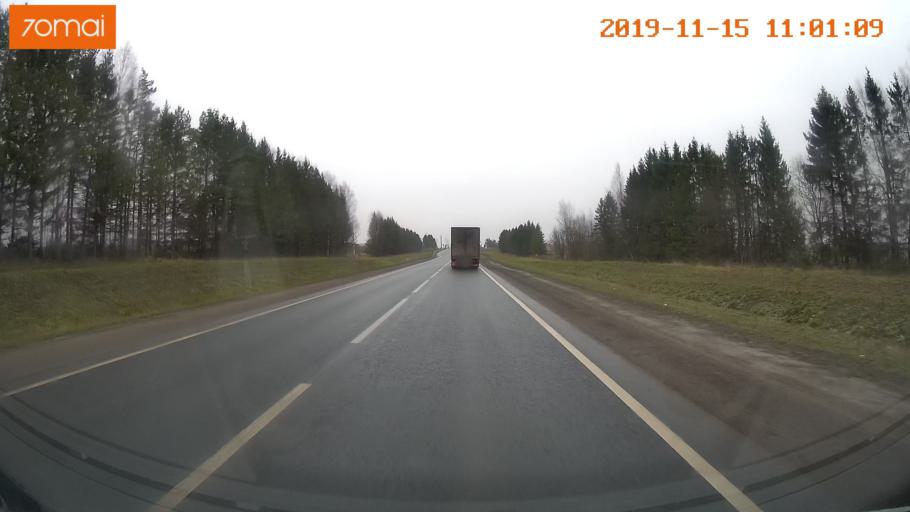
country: RU
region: Vologda
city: Chebsara
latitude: 59.1340
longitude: 38.9149
